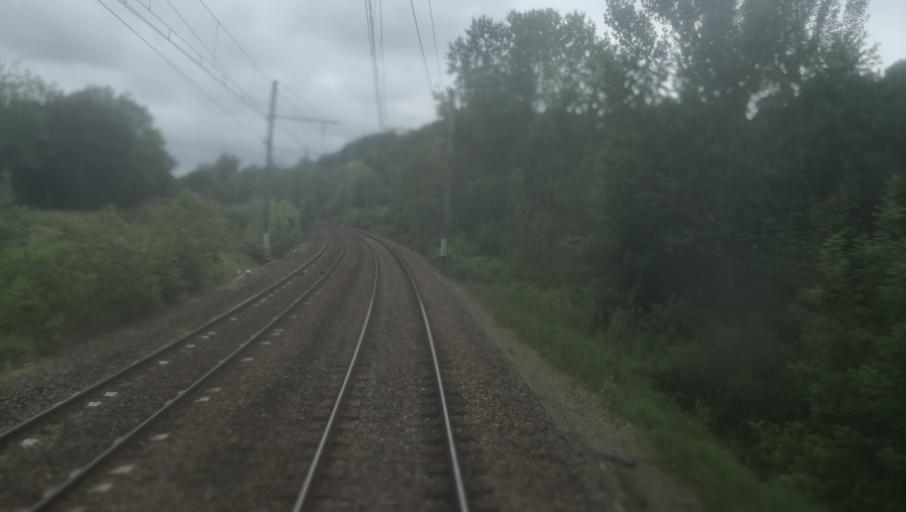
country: FR
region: Midi-Pyrenees
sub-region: Departement du Tarn-et-Garonne
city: Saint-Nicolas-de-la-Grave
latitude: 44.0942
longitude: 1.0239
